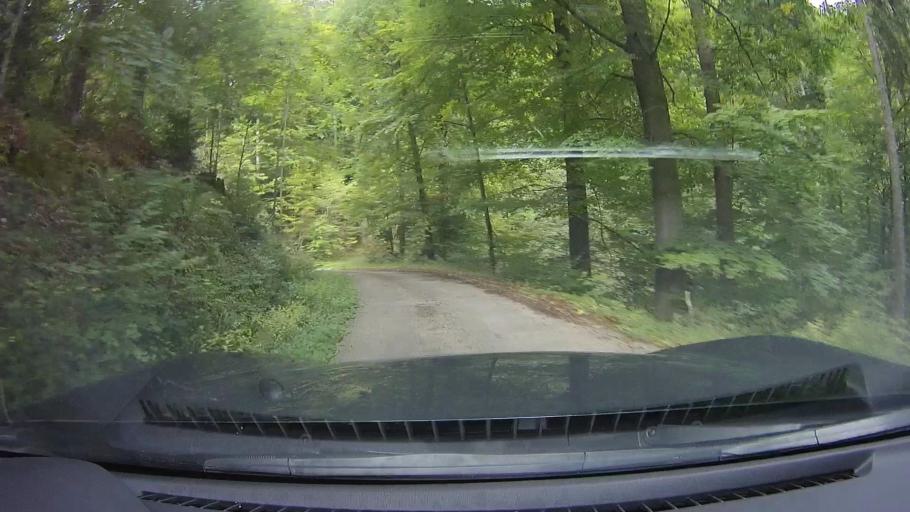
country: DE
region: Baden-Wuerttemberg
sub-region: Regierungsbezirk Stuttgart
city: Sulzbach an der Murr
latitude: 48.9796
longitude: 9.5193
